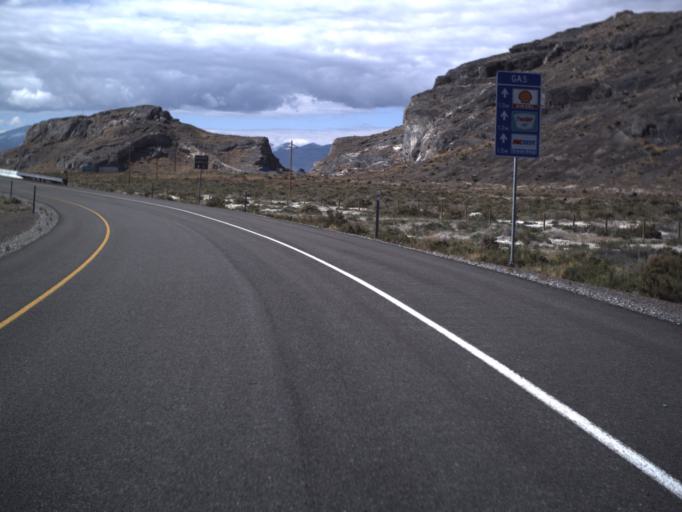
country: US
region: Utah
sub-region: Tooele County
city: Wendover
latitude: 40.7488
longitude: -114.0151
